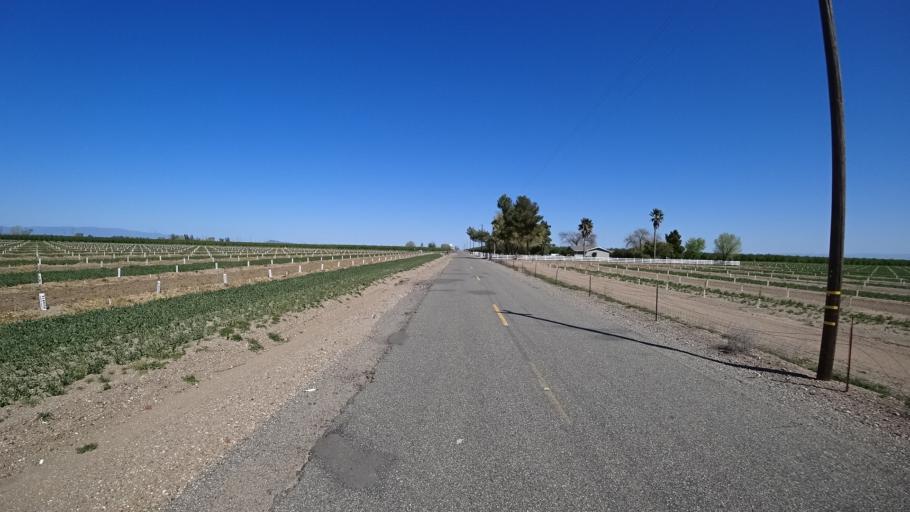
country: US
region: California
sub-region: Glenn County
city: Orland
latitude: 39.6376
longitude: -122.2534
